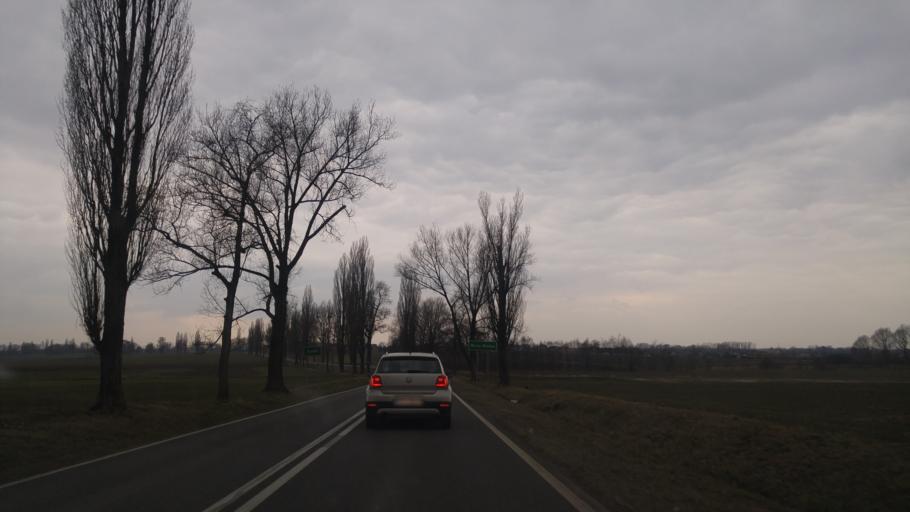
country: PL
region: Silesian Voivodeship
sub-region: Powiat pszczynski
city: Radostowice
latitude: 49.9528
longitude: 18.8776
